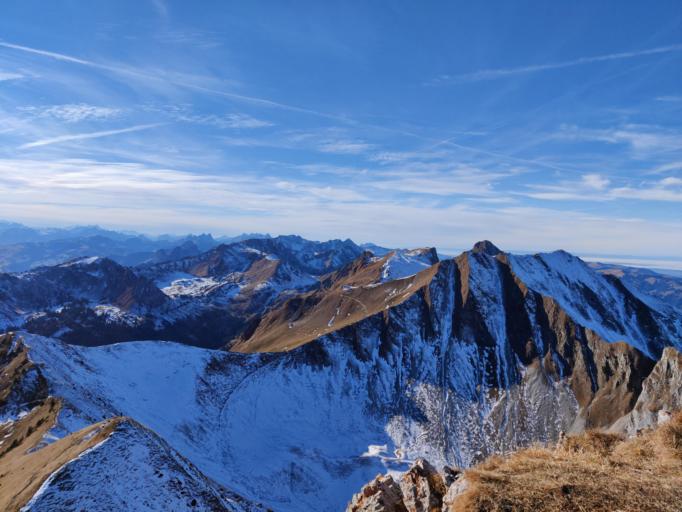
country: CH
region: Bern
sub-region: Thun District
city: Blumenstein
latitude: 46.7047
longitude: 7.4508
